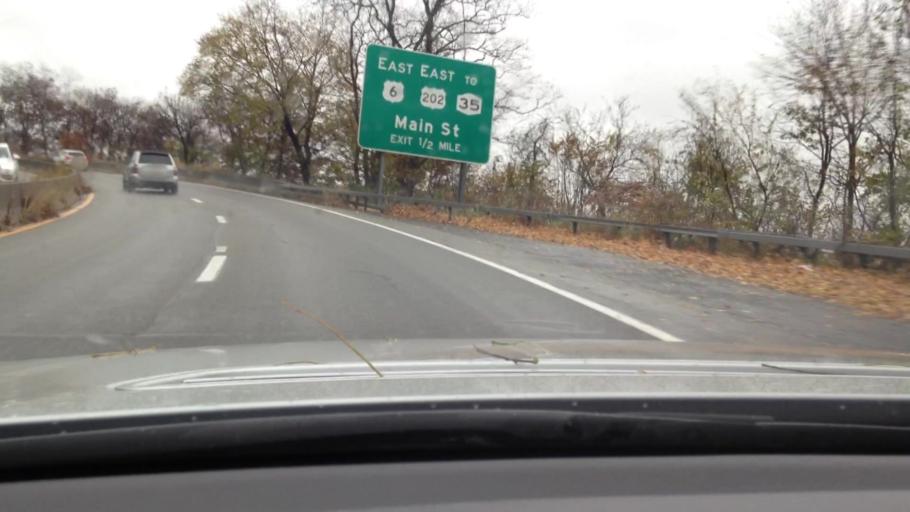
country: US
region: New York
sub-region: Westchester County
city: Peekskill
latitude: 41.2934
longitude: -73.9351
